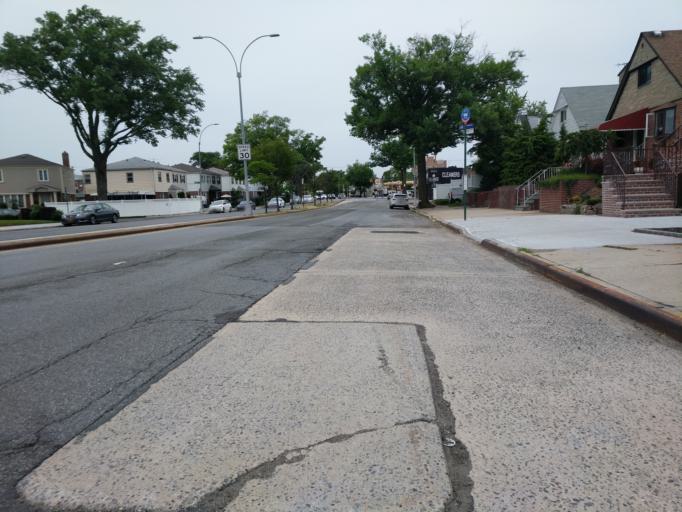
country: US
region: New York
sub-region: Nassau County
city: East Atlantic Beach
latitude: 40.7520
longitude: -73.7798
